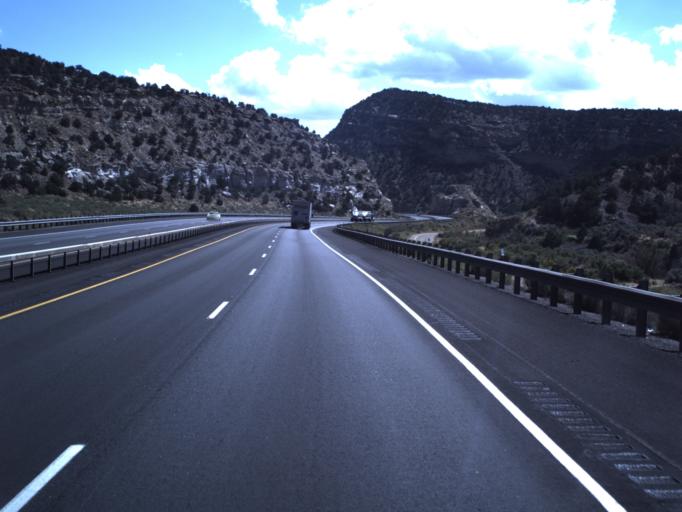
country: US
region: Utah
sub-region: Sevier County
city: Salina
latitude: 38.9130
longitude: -111.7158
